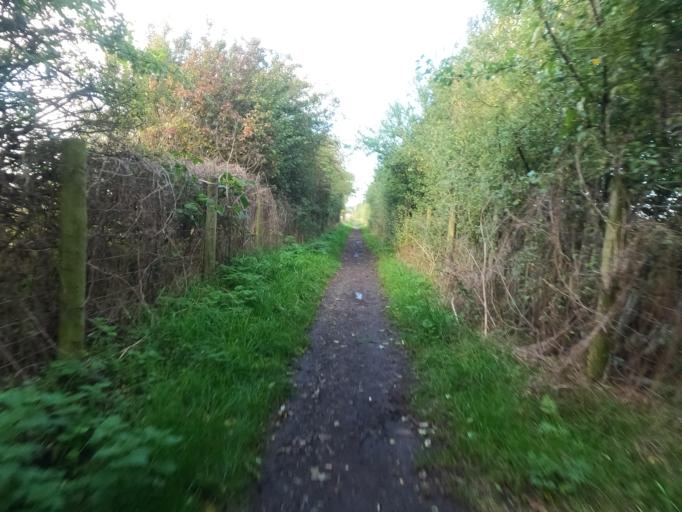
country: GB
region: England
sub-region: Northumberland
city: Seghill
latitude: 55.0708
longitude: -1.5403
